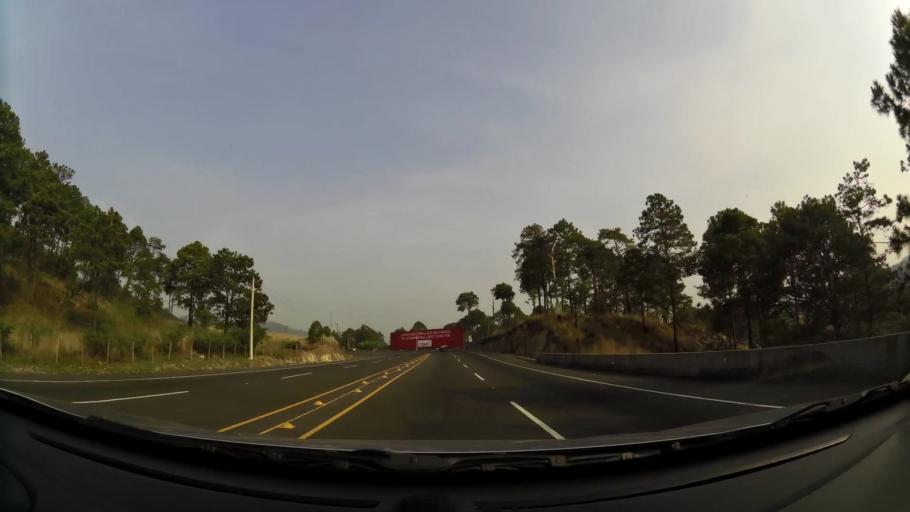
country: HN
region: Francisco Morazan
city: Zambrano
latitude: 14.2514
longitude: -87.3765
